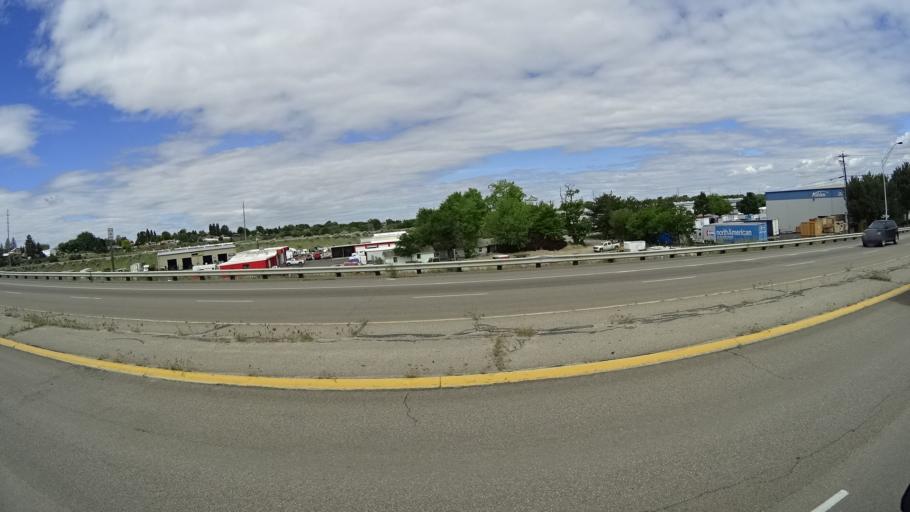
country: US
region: Idaho
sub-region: Ada County
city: Boise
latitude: 43.5710
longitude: -116.1936
